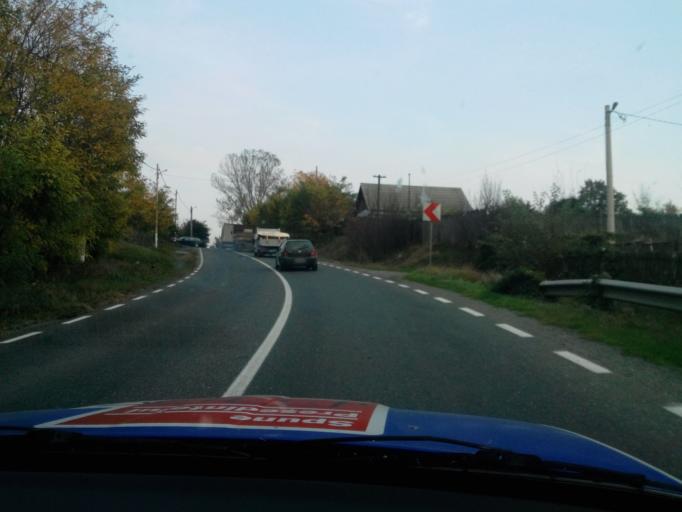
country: RO
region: Tulcea
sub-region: Comuna Somova
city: Somova
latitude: 45.1787
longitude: 28.6749
